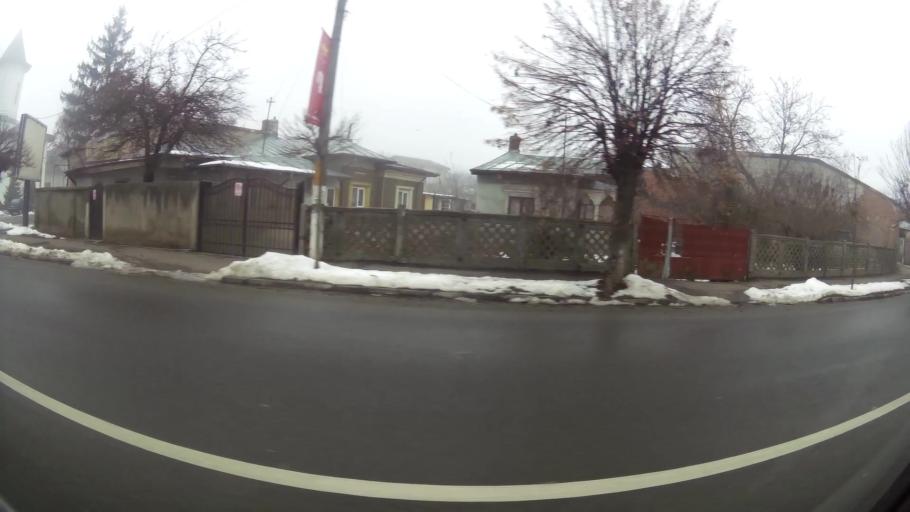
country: RO
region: Ilfov
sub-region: Comuna Chiajna
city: Chiajna
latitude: 44.4613
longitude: 25.9774
